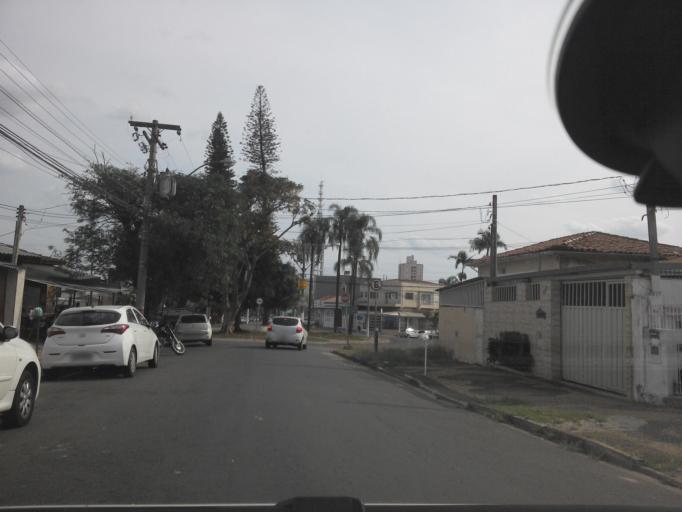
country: BR
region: Sao Paulo
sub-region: Campinas
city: Campinas
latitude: -22.8942
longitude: -47.0799
